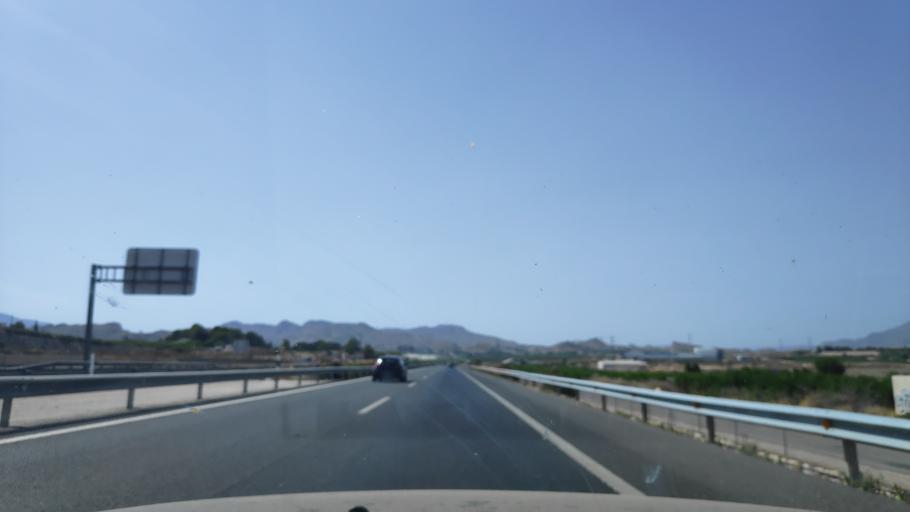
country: ES
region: Murcia
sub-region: Murcia
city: Archena
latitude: 38.1301
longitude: -1.2626
